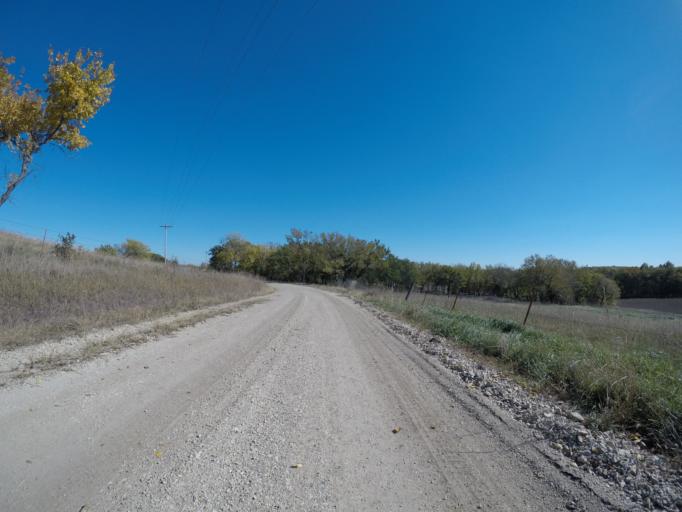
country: US
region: Kansas
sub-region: Wabaunsee County
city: Alma
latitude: 38.9826
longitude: -96.4609
